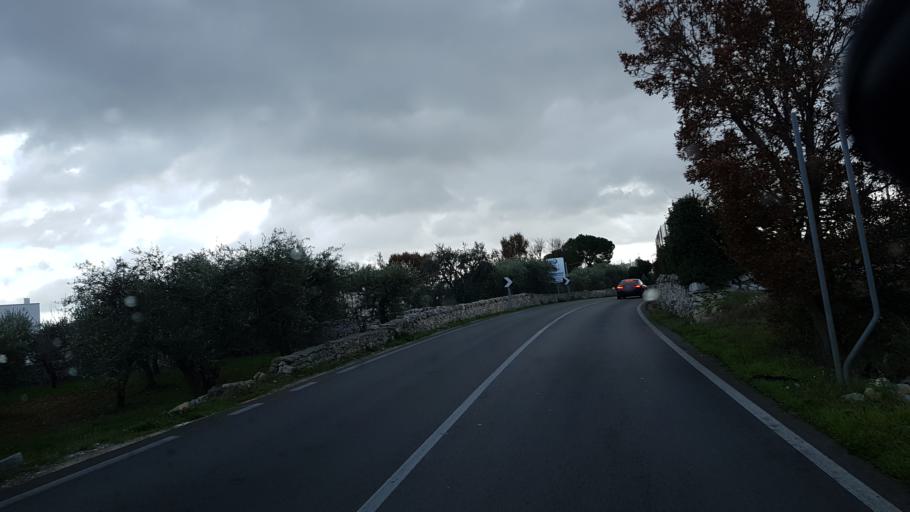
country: IT
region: Apulia
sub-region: Provincia di Bari
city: Locorotondo
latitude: 40.7655
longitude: 17.3326
